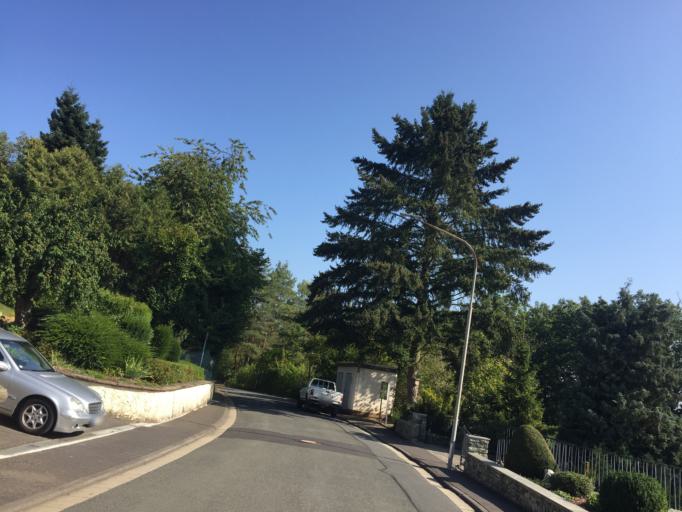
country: DE
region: Hesse
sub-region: Regierungsbezirk Giessen
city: Schoeffengrund
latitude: 50.4525
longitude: 8.5563
